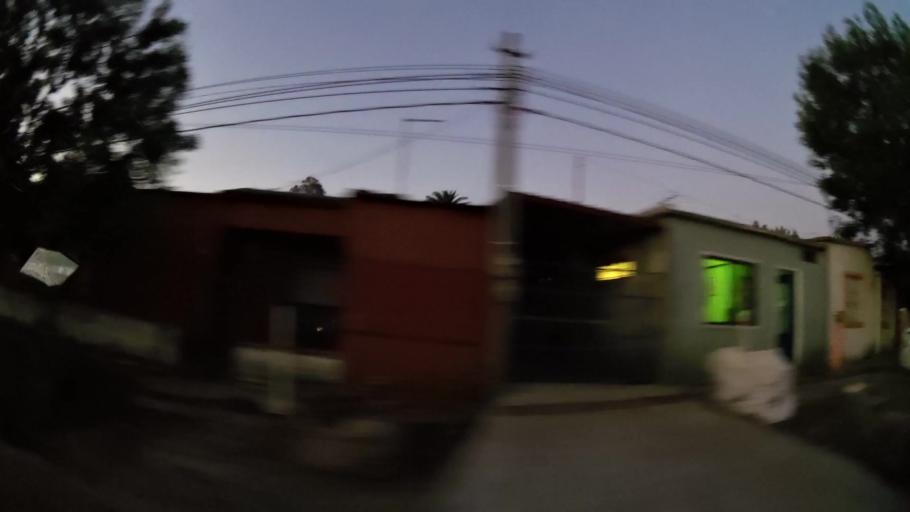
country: UY
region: Canelones
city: La Paz
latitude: -34.8253
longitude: -56.1793
